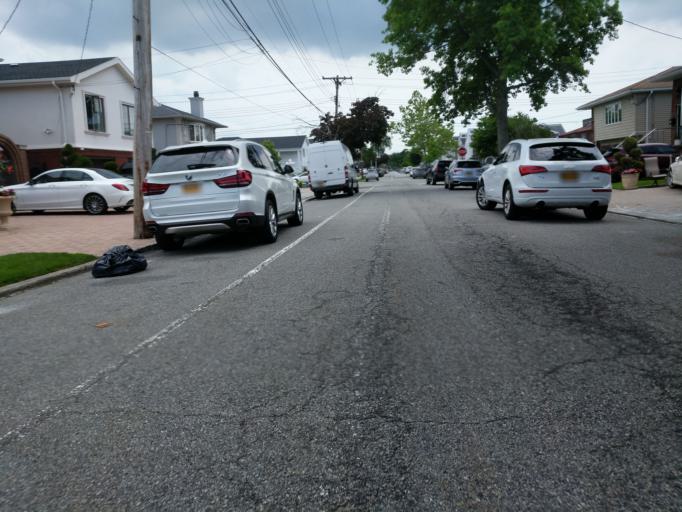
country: US
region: New York
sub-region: Queens County
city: Borough of Queens
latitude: 40.6544
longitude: -73.8407
